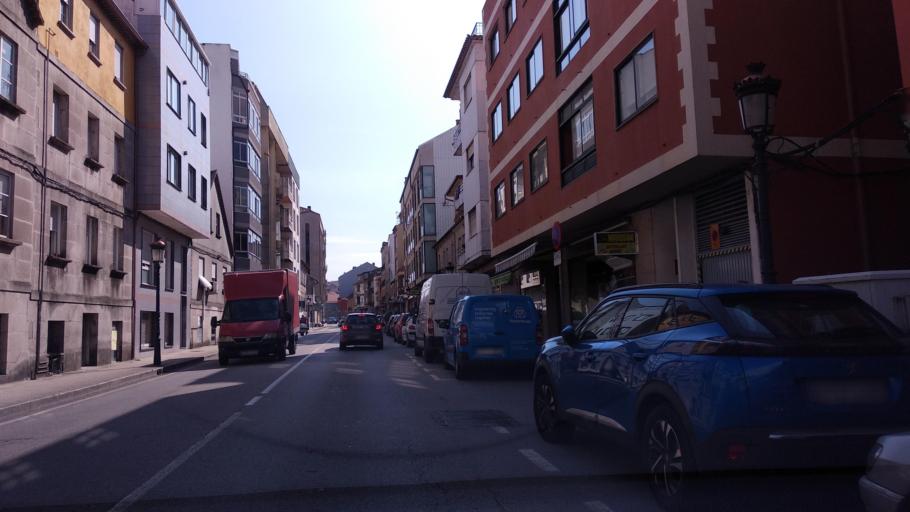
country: ES
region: Galicia
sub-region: Provincia de Pontevedra
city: Moana
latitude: 42.2848
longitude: -8.7347
